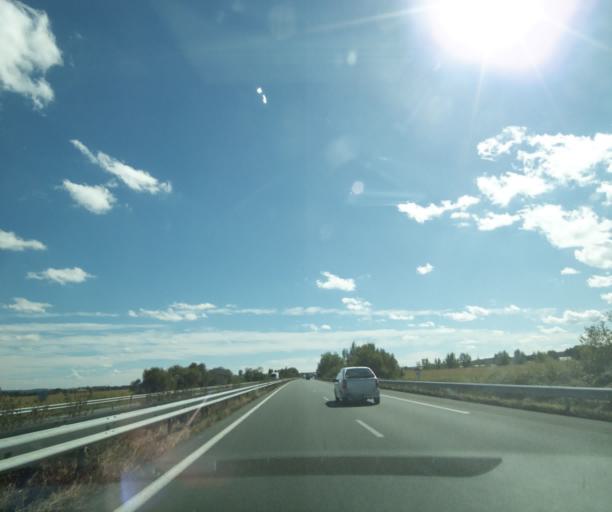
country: FR
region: Aquitaine
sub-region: Departement du Lot-et-Garonne
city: Damazan
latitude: 44.3321
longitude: 0.2561
